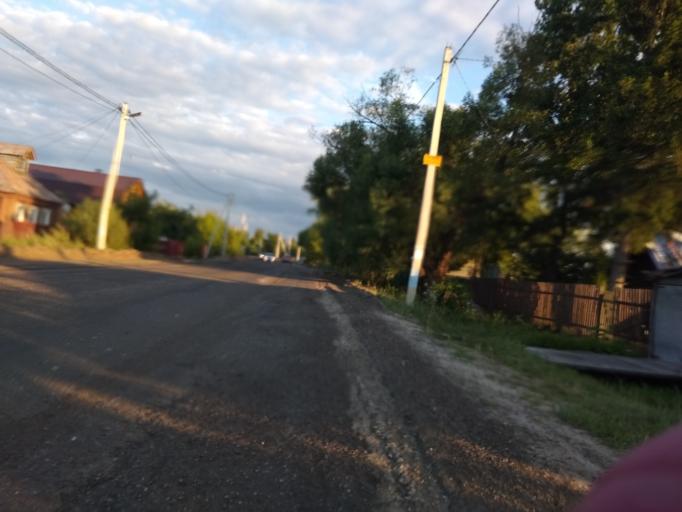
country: RU
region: Moskovskaya
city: Misheronskiy
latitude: 55.6556
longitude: 39.7521
